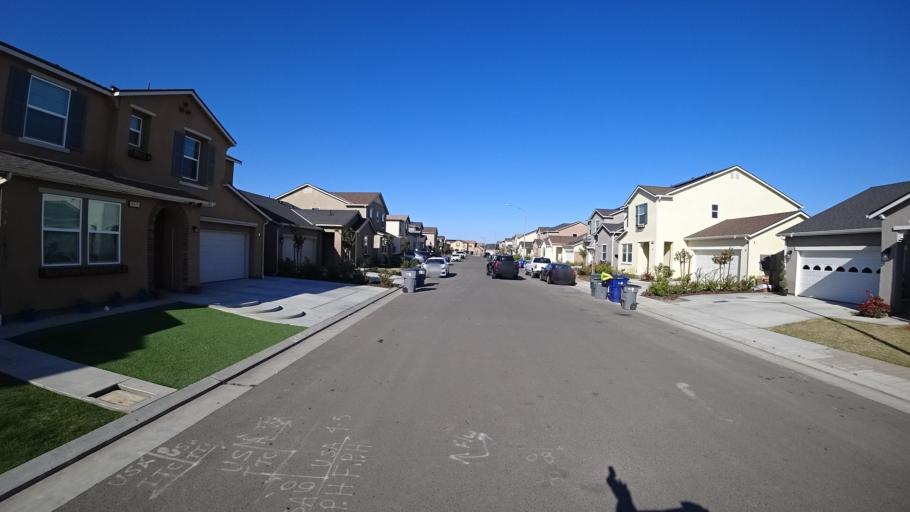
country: US
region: California
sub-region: Fresno County
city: West Park
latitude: 36.8003
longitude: -119.9042
